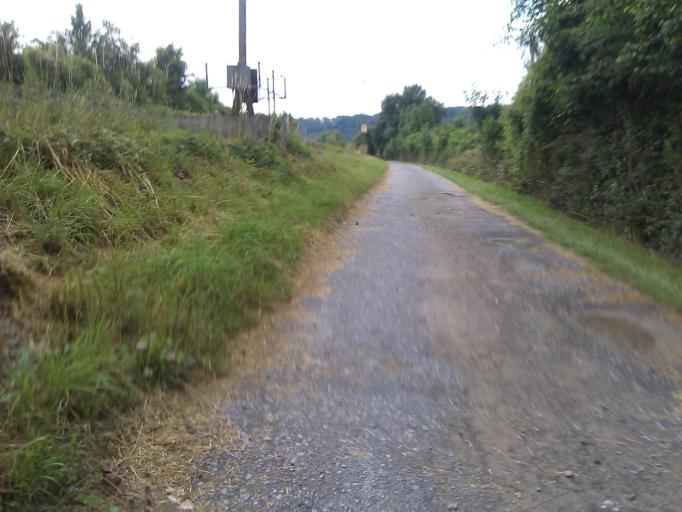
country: DE
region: Baden-Wuerttemberg
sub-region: Regierungsbezirk Stuttgart
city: Lauffen am Neckar
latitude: 49.0644
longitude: 9.1332
